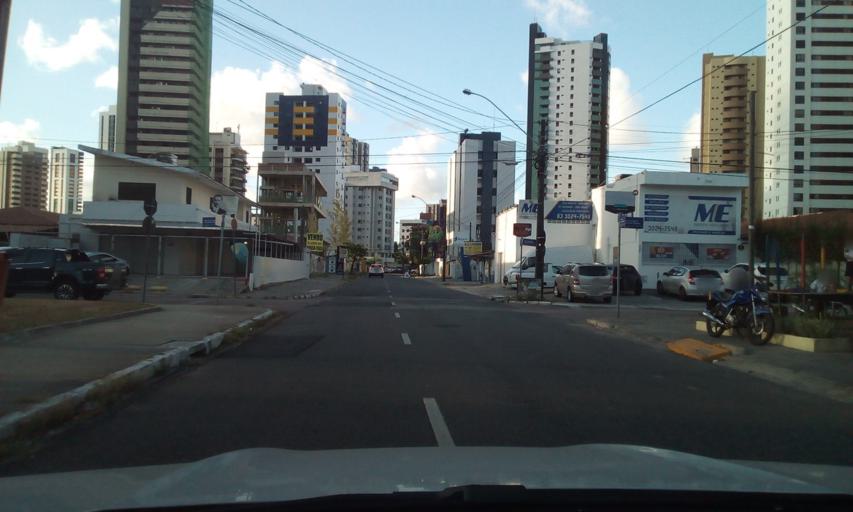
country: BR
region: Paraiba
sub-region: Joao Pessoa
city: Joao Pessoa
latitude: -7.1016
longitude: -34.8381
